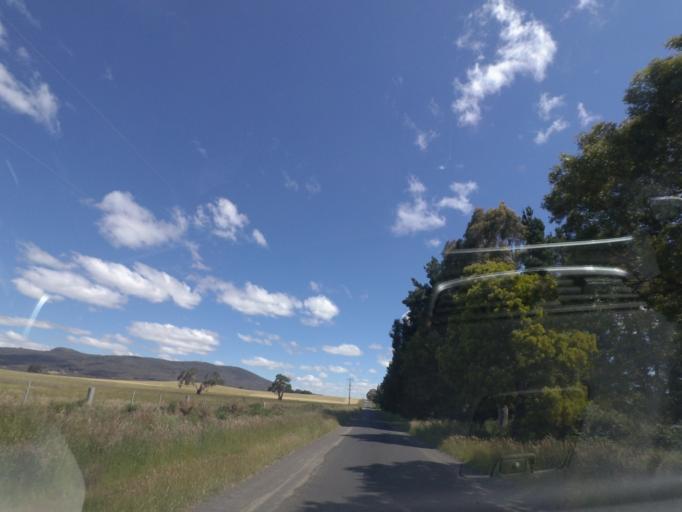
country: AU
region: Victoria
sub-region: Hume
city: Sunbury
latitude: -37.3269
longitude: 144.5595
